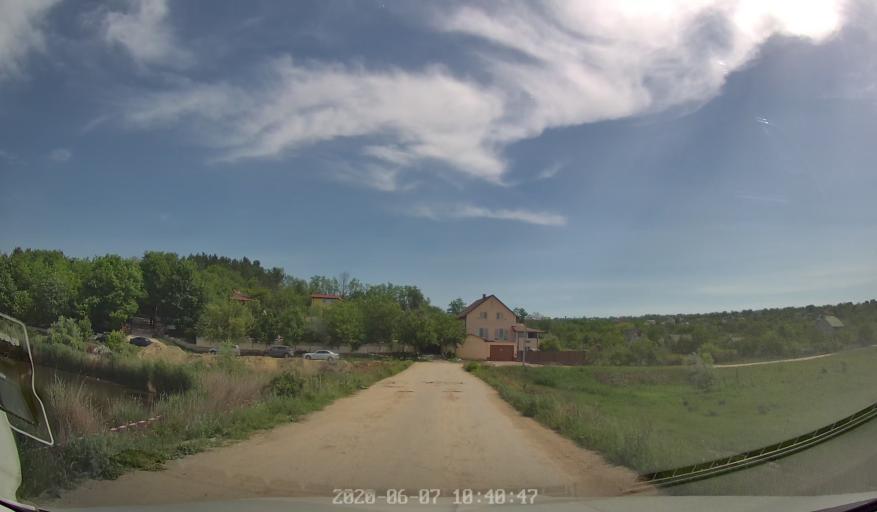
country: MD
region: Laloveni
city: Ialoveni
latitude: 46.9814
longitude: 28.7050
